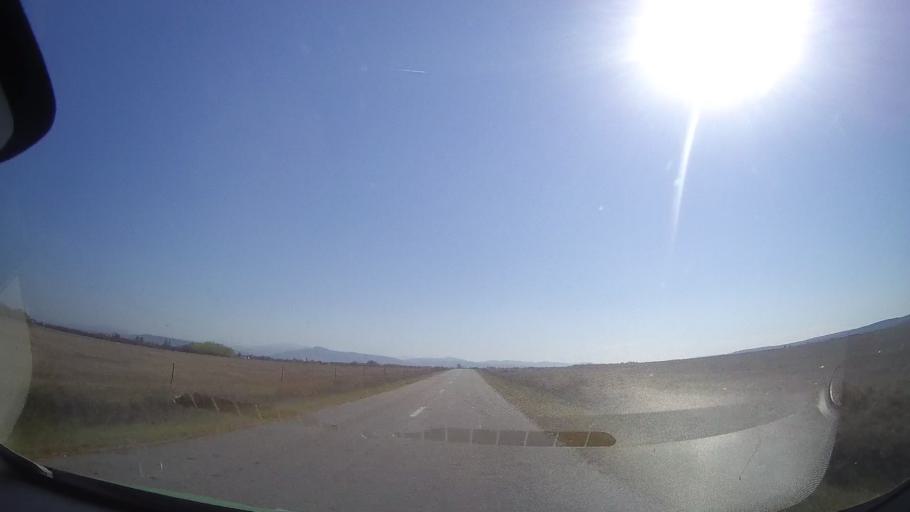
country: RO
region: Timis
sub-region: Comuna Traian Vuia
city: Traian Vuia
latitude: 45.7968
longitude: 22.0128
